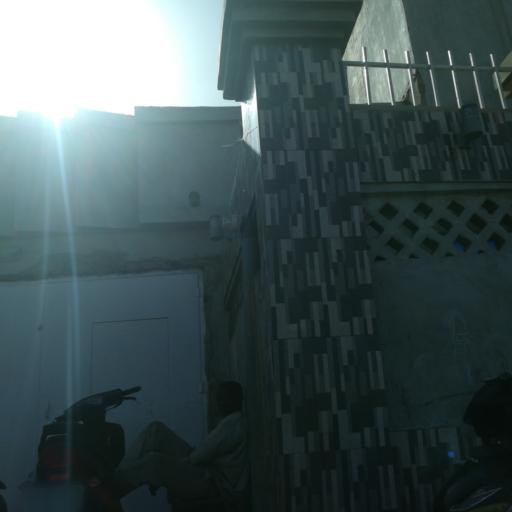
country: NG
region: Kano
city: Kano
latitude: 12.0158
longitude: 8.5161
